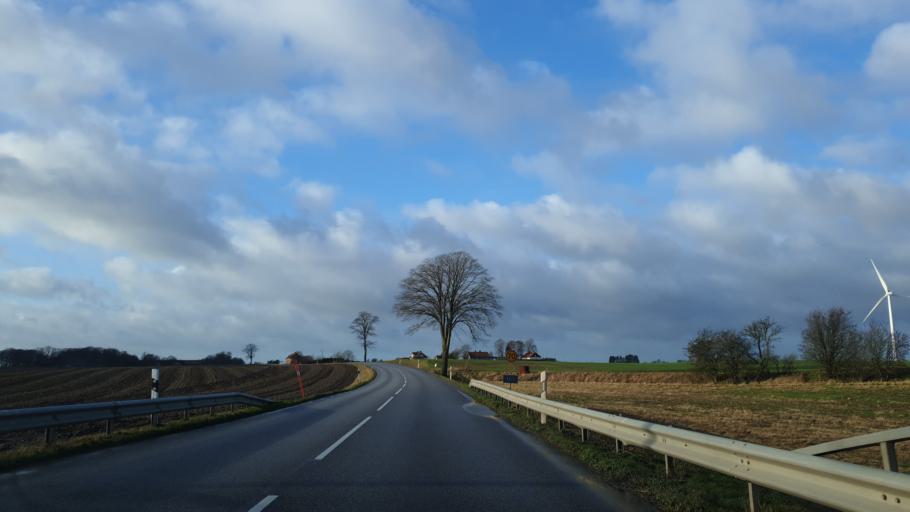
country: SE
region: Skane
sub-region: Trelleborgs Kommun
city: Anderslov
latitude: 55.4226
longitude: 13.4078
